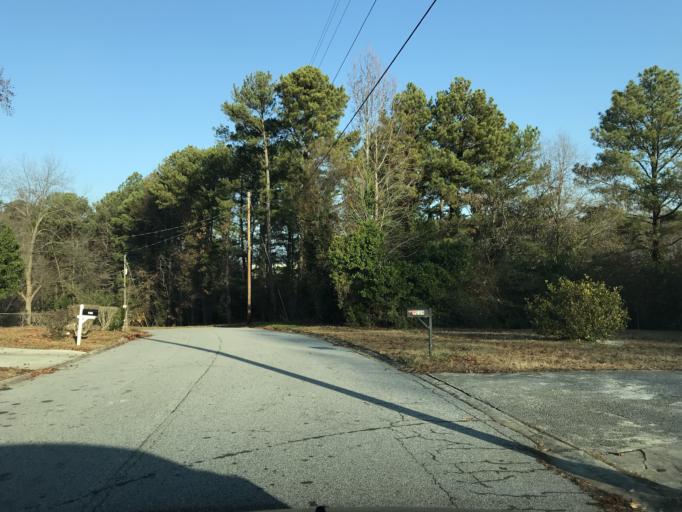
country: US
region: Georgia
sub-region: Fulton County
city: College Park
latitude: 33.6142
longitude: -84.4295
